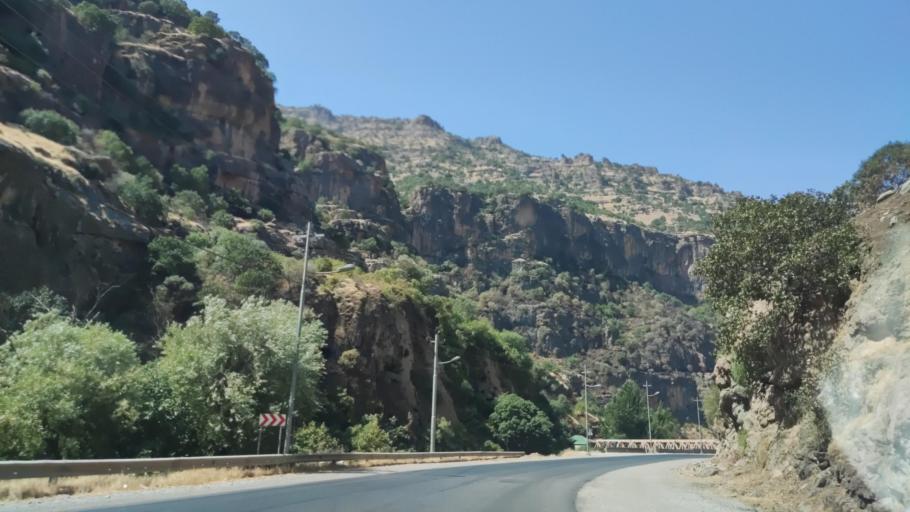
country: IQ
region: Arbil
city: Ruwandiz
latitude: 36.6270
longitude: 44.4676
